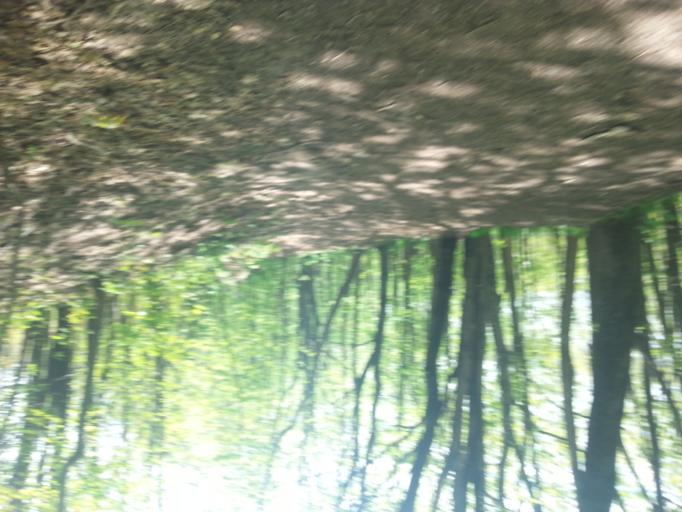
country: CA
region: Quebec
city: Quebec
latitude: 46.7714
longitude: -71.2553
